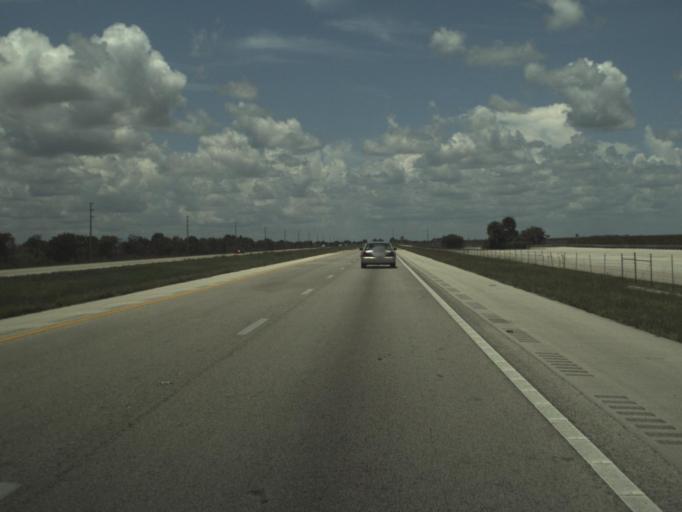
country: US
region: Florida
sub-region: Broward County
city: Weston
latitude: 26.1466
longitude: -80.6796
